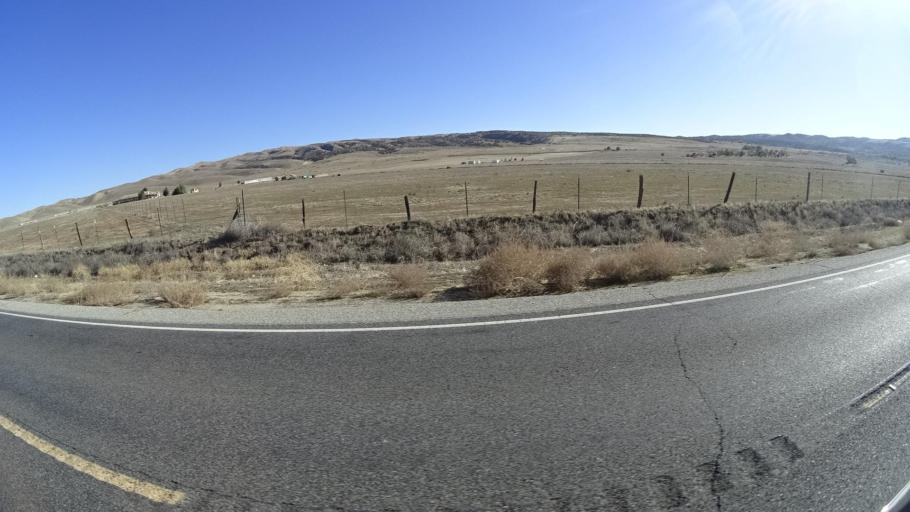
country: US
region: California
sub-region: Kern County
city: Maricopa
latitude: 34.9436
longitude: -119.4621
